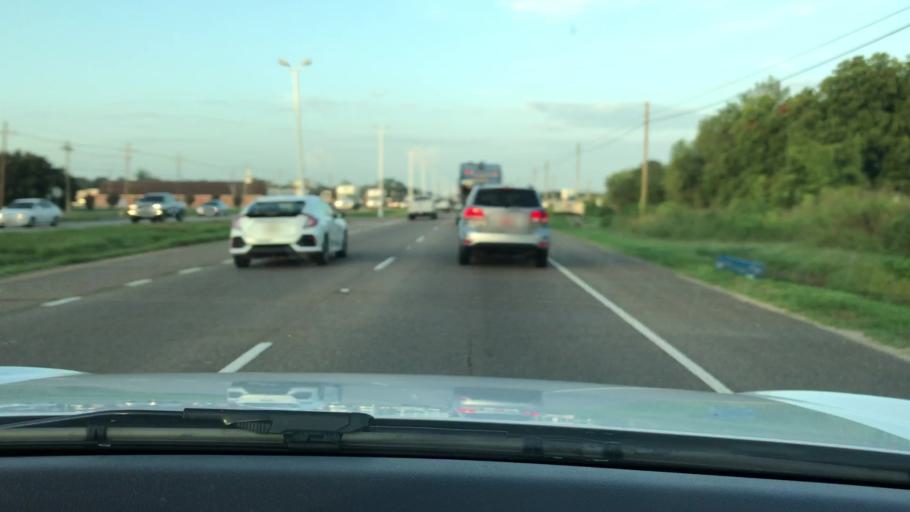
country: US
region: Louisiana
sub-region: West Baton Rouge Parish
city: Brusly
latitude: 30.3774
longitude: -91.2519
